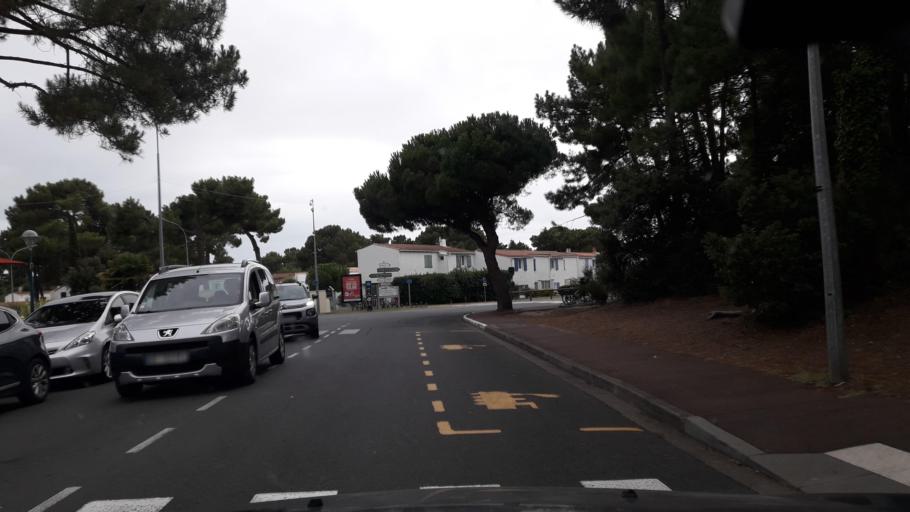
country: FR
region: Poitou-Charentes
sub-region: Departement de la Charente-Maritime
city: Les Mathes
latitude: 45.6898
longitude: -1.1812
